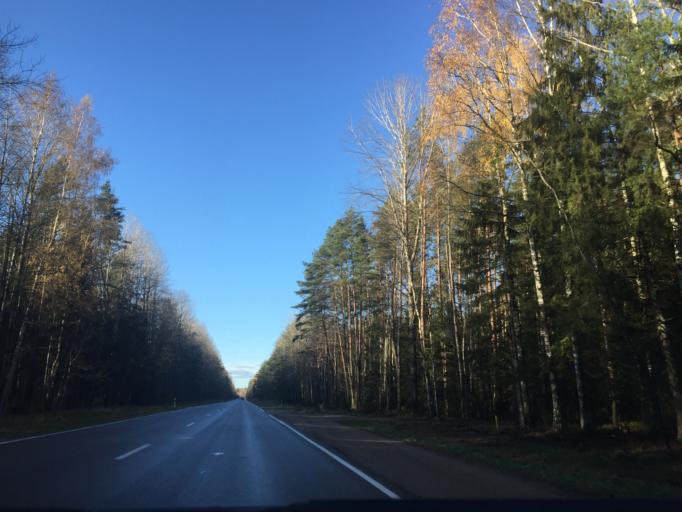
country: LV
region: Engure
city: Smarde
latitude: 56.9235
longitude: 23.4156
